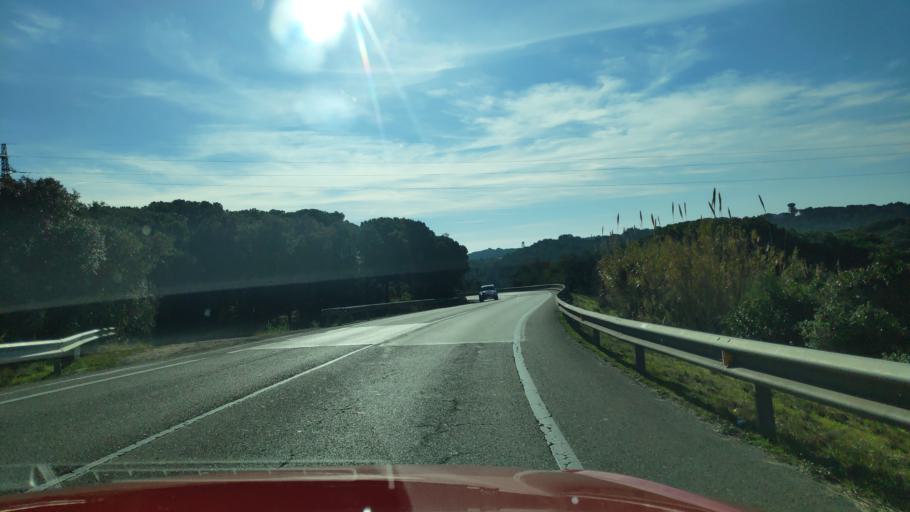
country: ES
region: Catalonia
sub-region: Provincia de Girona
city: Lloret de Mar
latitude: 41.7201
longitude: 2.8255
